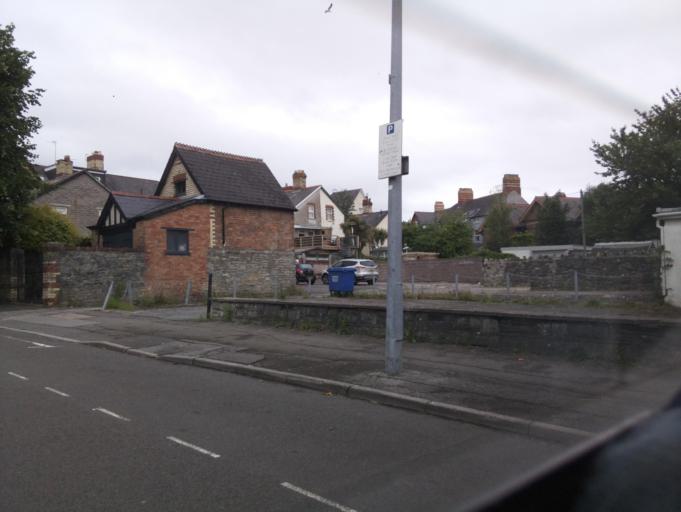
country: GB
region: Wales
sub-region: Vale of Glamorgan
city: Penarth
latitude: 51.4377
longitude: -3.1748
